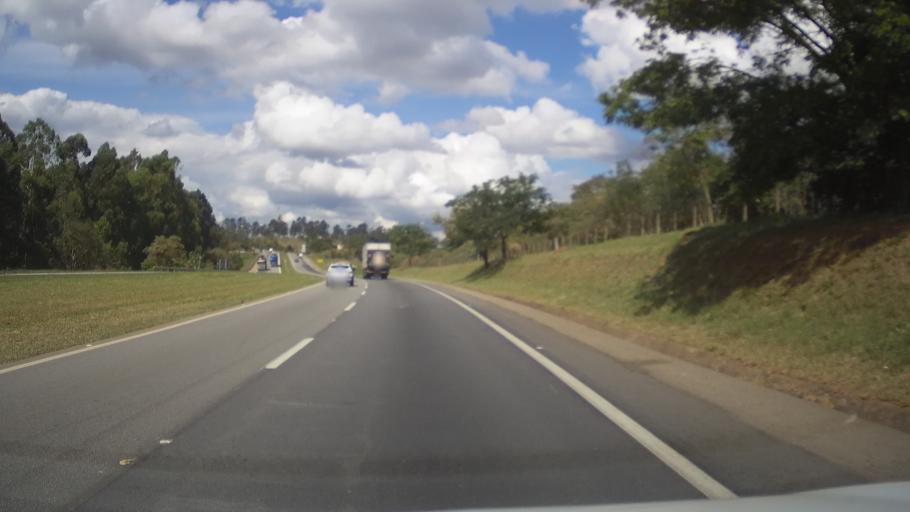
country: BR
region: Minas Gerais
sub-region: Oliveira
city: Oliveira
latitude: -20.8287
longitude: -44.8087
